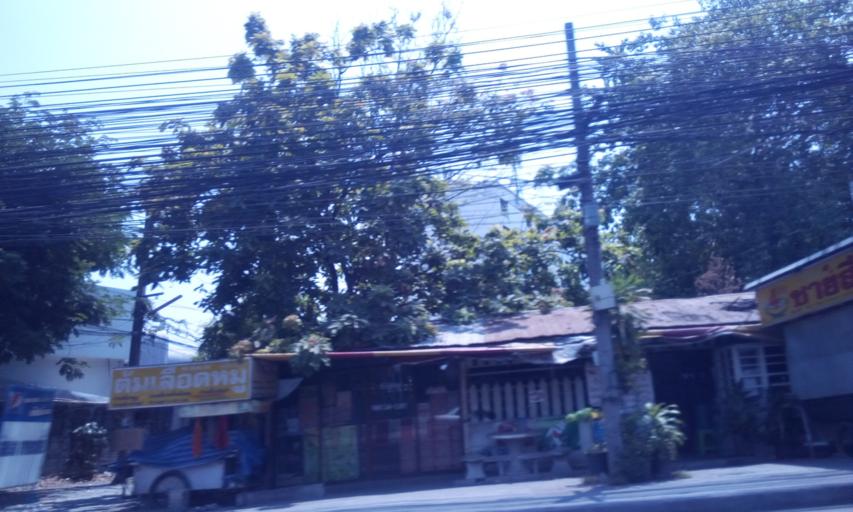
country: TH
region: Nonthaburi
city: Pak Kret
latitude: 13.9069
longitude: 100.5097
